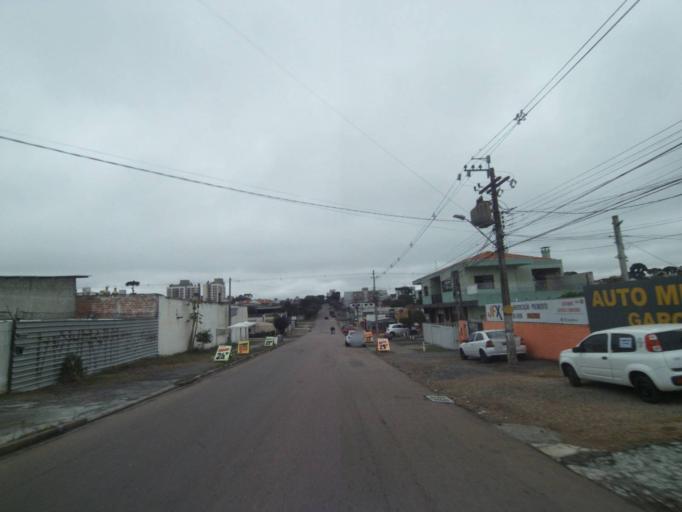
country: BR
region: Parana
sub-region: Curitiba
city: Curitiba
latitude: -25.5155
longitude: -49.2990
